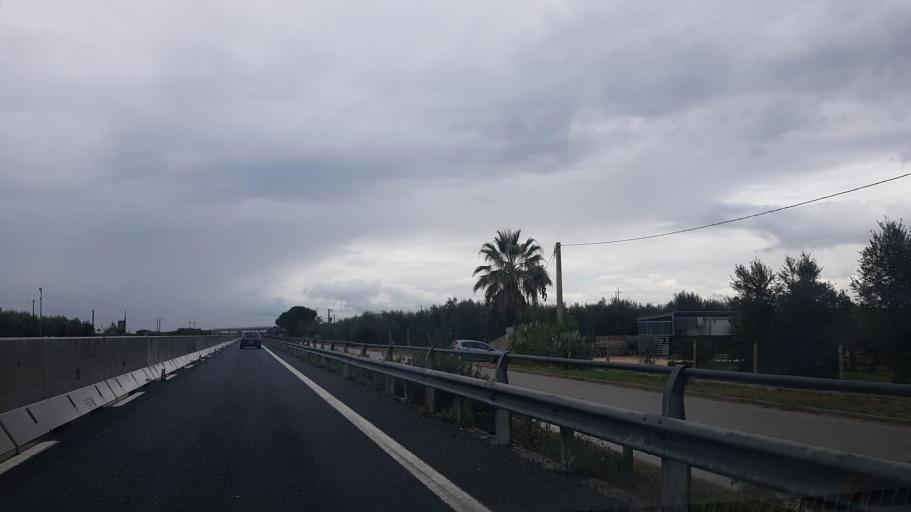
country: IT
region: Apulia
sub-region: Provincia di Taranto
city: Massafra
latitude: 40.5285
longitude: 17.1220
